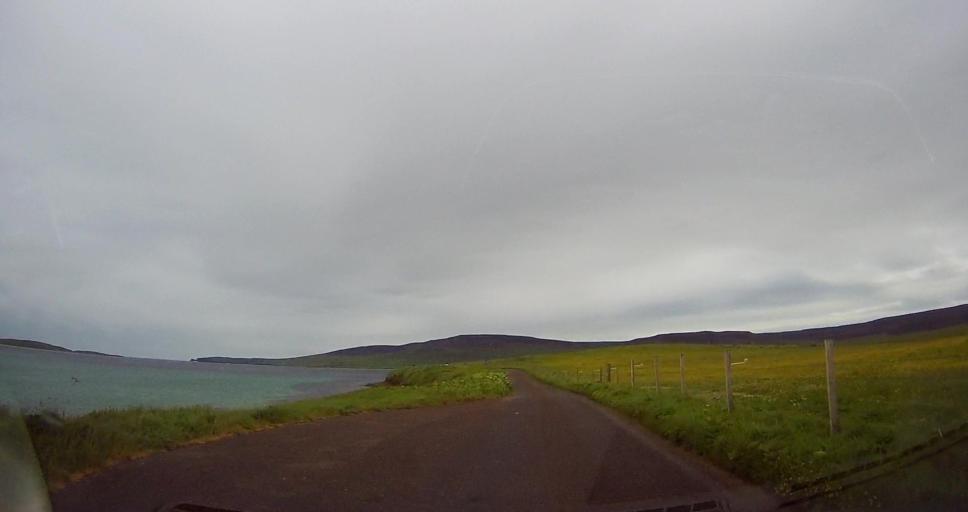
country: GB
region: Scotland
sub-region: Orkney Islands
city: Orkney
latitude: 59.1202
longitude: -3.0856
